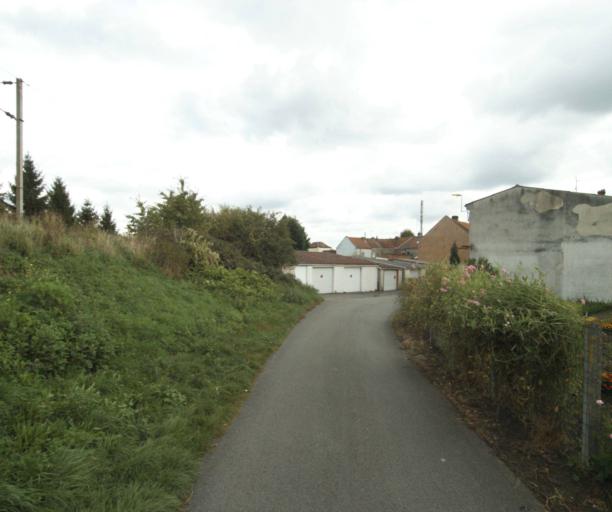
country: FR
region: Nord-Pas-de-Calais
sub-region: Departement du Nord
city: Lompret
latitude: 50.6657
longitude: 2.9869
